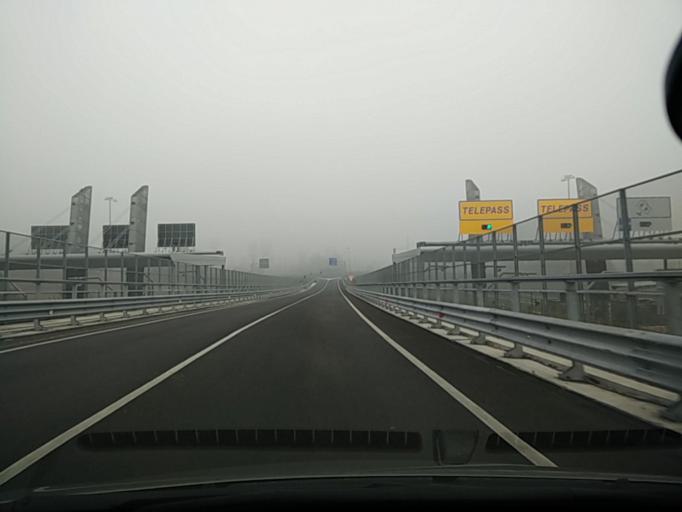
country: IT
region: Veneto
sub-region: Provincia di Venezia
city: Martellago
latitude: 45.5589
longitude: 12.1528
